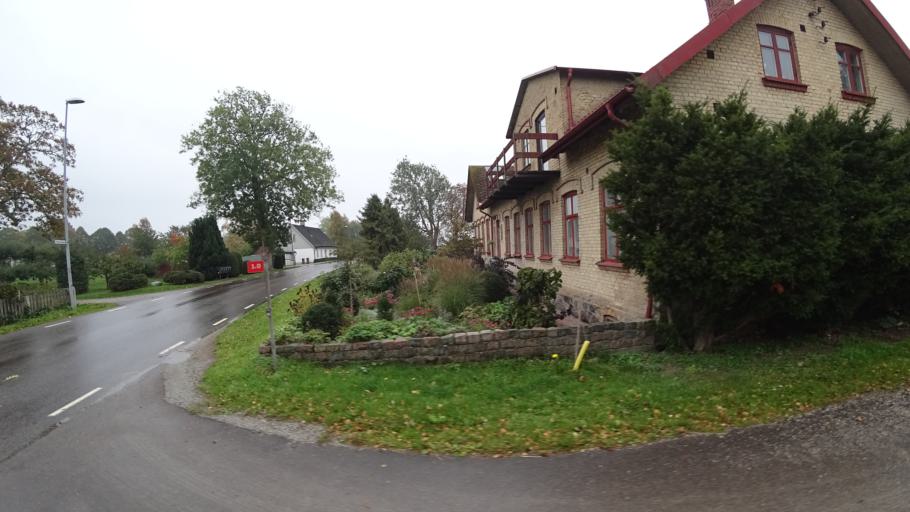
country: SE
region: Skane
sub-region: Kavlinge Kommun
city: Kaevlinge
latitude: 55.8063
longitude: 13.1513
